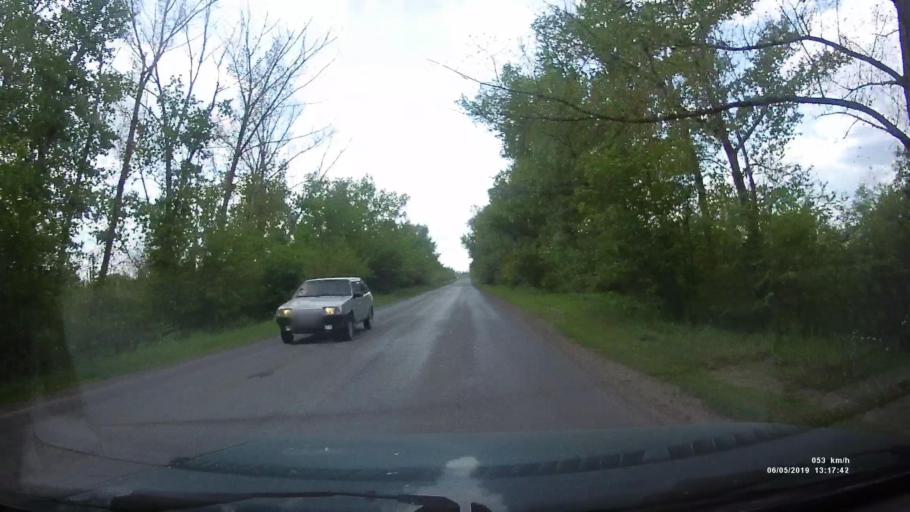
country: RU
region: Rostov
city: Ust'-Donetskiy
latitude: 47.7387
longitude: 40.9209
